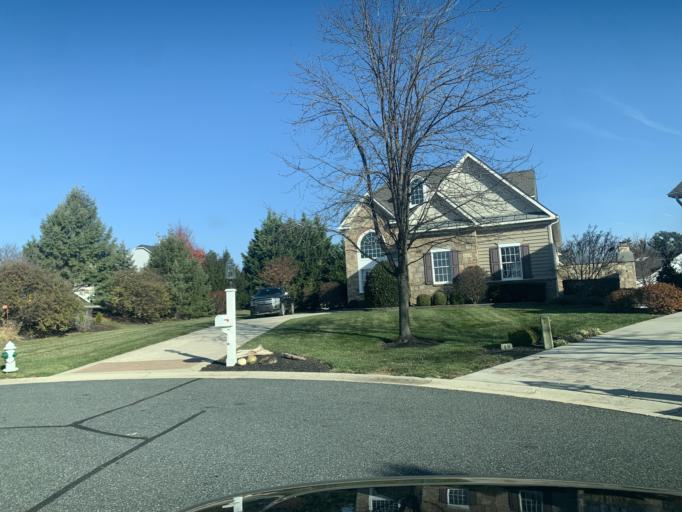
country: US
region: Maryland
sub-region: Harford County
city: Havre de Grace
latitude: 39.5540
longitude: -76.1265
